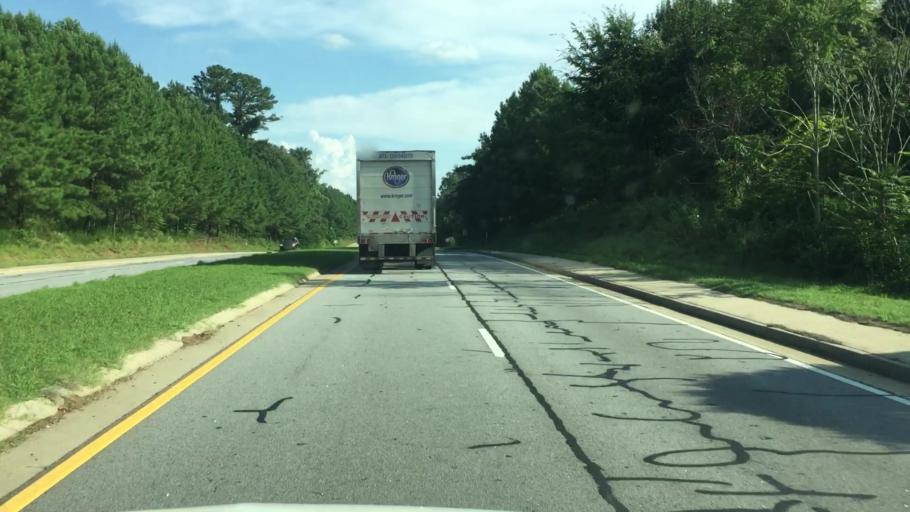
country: US
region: Georgia
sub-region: Rockdale County
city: Lakeview Estates
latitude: 33.7824
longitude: -84.0473
